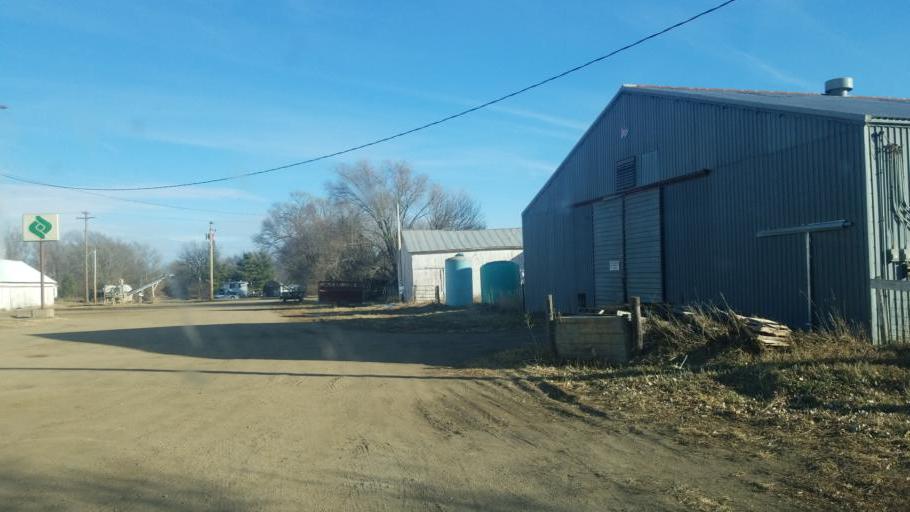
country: US
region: South Dakota
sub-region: Charles Mix County
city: Wagner
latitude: 42.8278
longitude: -98.4690
